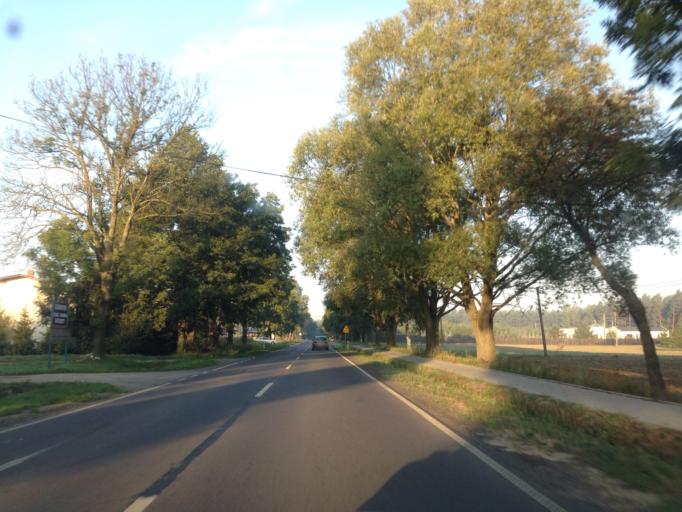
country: PL
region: Kujawsko-Pomorskie
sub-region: Powiat golubsko-dobrzynski
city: Golub-Dobrzyn
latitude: 53.1094
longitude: 19.1035
